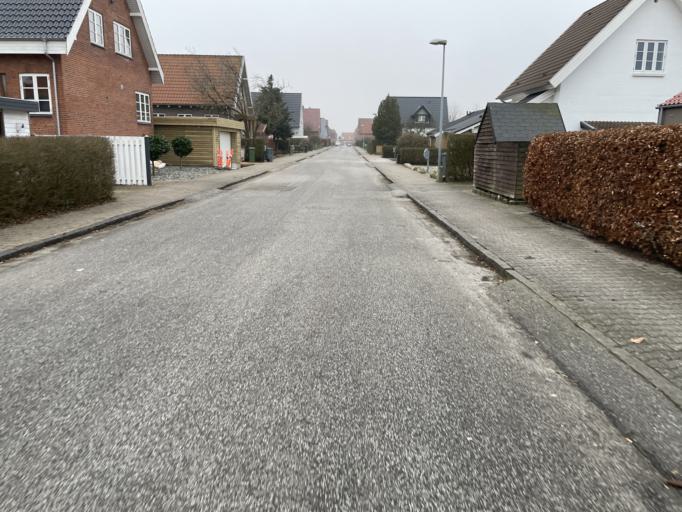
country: DK
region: South Denmark
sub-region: Fredericia Kommune
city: Fredericia
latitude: 55.5772
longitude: 9.7565
